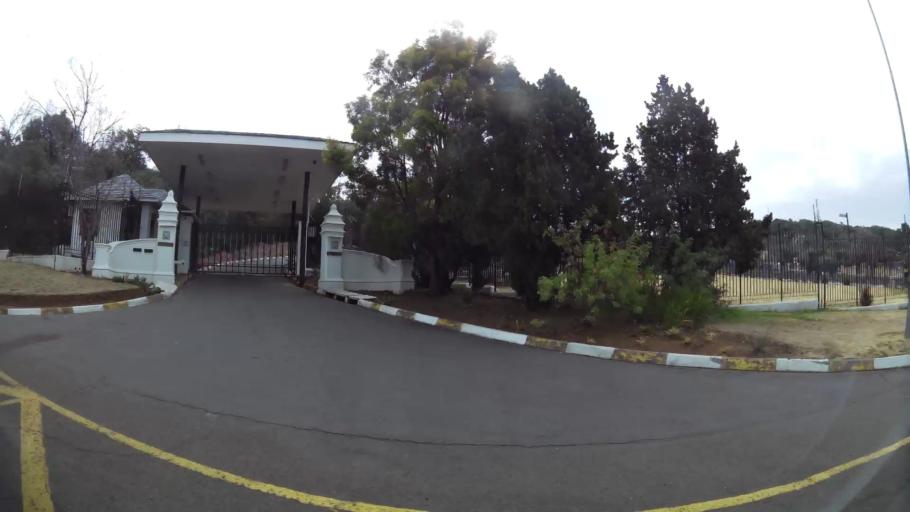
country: ZA
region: Orange Free State
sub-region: Mangaung Metropolitan Municipality
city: Bloemfontein
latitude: -29.1005
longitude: 26.2176
